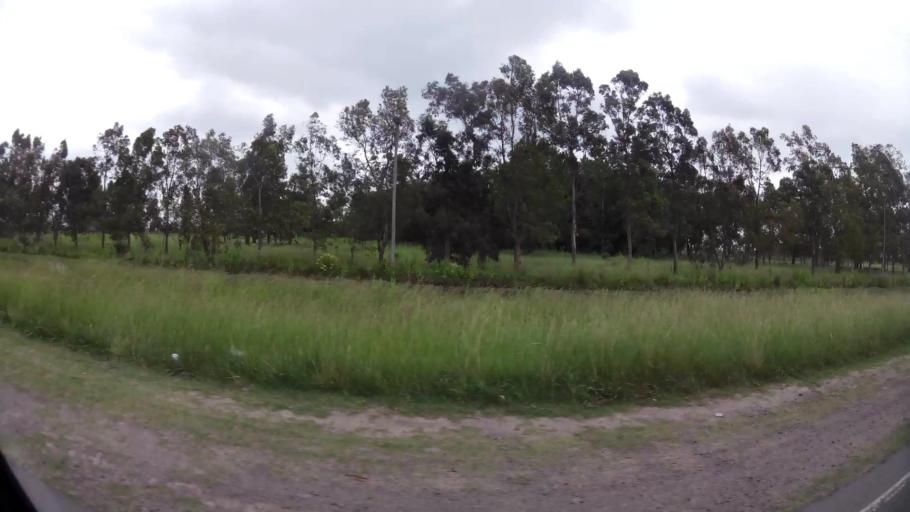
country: AR
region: Buenos Aires
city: Guernica
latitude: -34.9507
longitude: -58.4638
